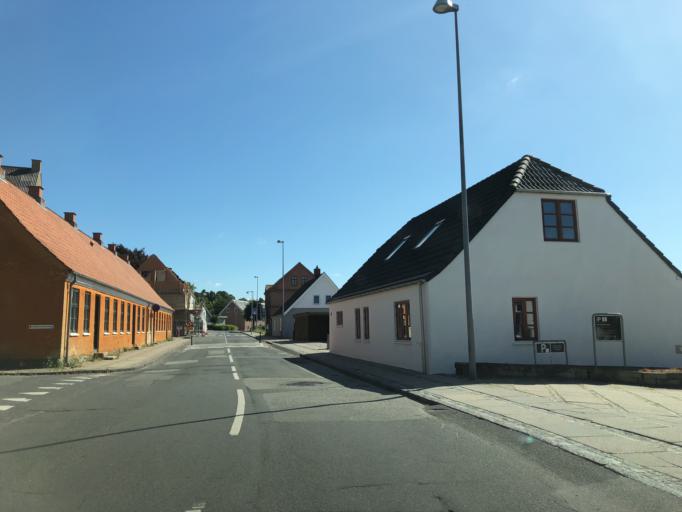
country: DK
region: North Denmark
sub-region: Mariagerfjord Kommune
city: Hobro
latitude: 56.6367
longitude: 9.7928
